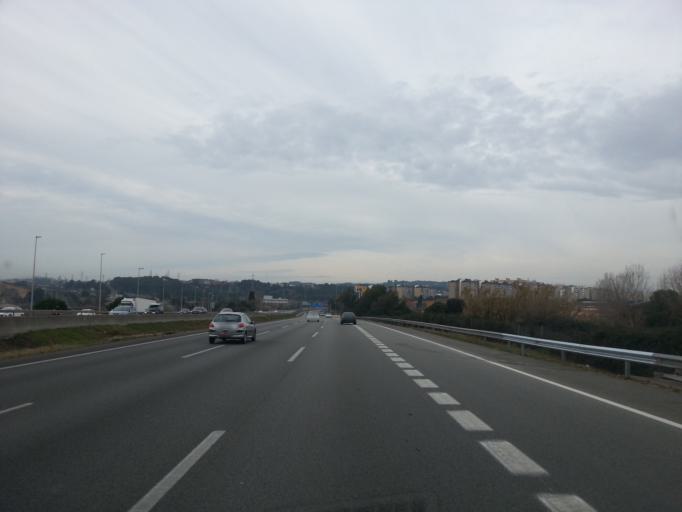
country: ES
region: Catalonia
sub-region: Provincia de Barcelona
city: Barbera del Valles
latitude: 41.5056
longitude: 2.1294
